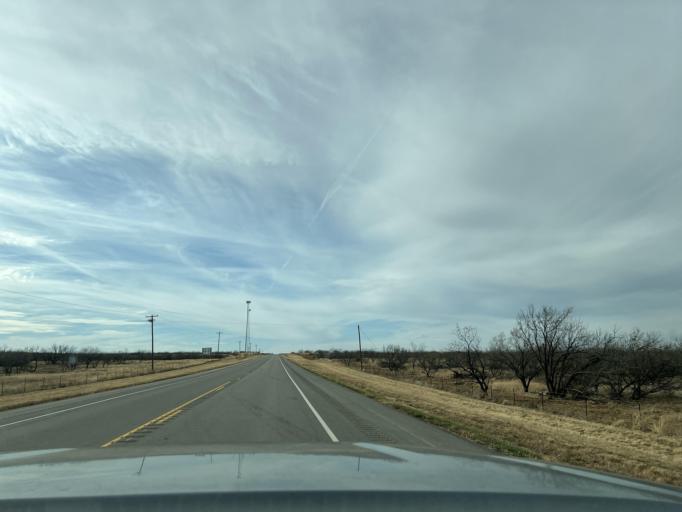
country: US
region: Texas
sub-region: Jones County
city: Anson
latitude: 32.7508
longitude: -99.7190
